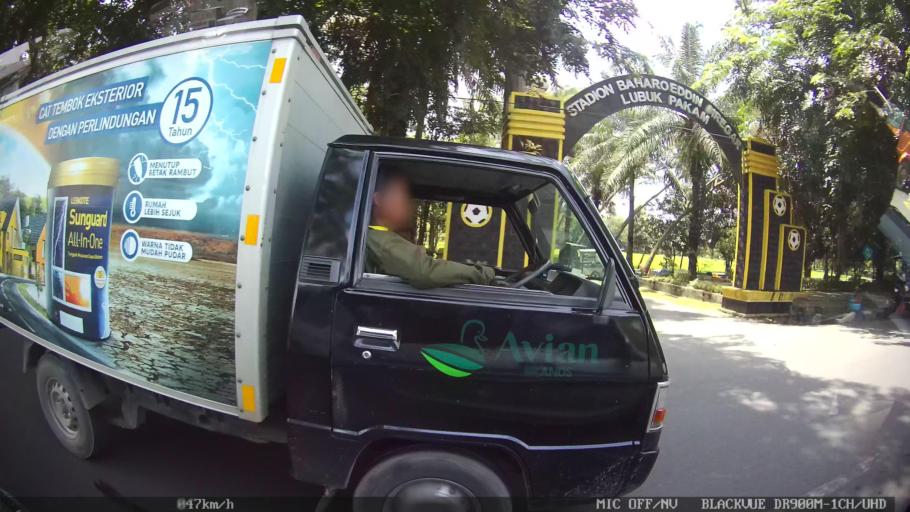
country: ID
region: North Sumatra
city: Percut
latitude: 3.5517
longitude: 98.8642
